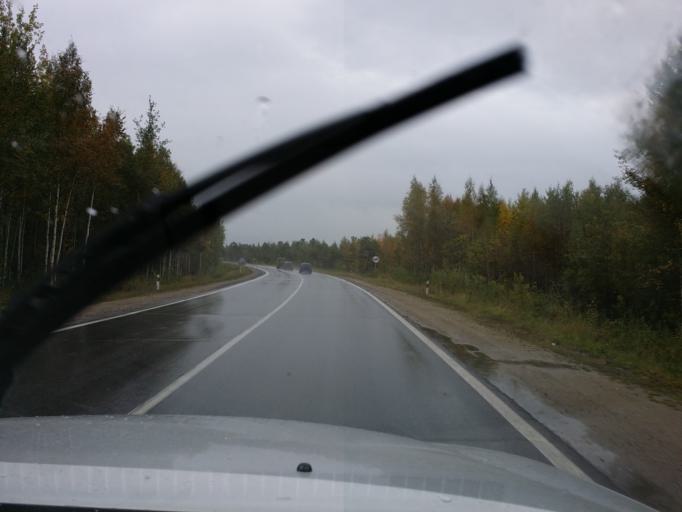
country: RU
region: Khanty-Mansiyskiy Avtonomnyy Okrug
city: Langepas
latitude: 61.1587
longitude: 75.6046
